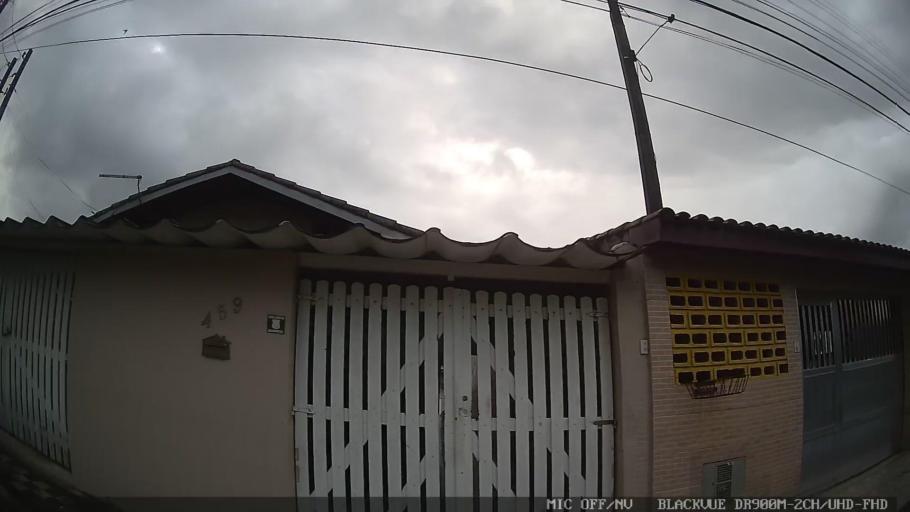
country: BR
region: Sao Paulo
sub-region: Itanhaem
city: Itanhaem
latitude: -24.1799
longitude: -46.7838
